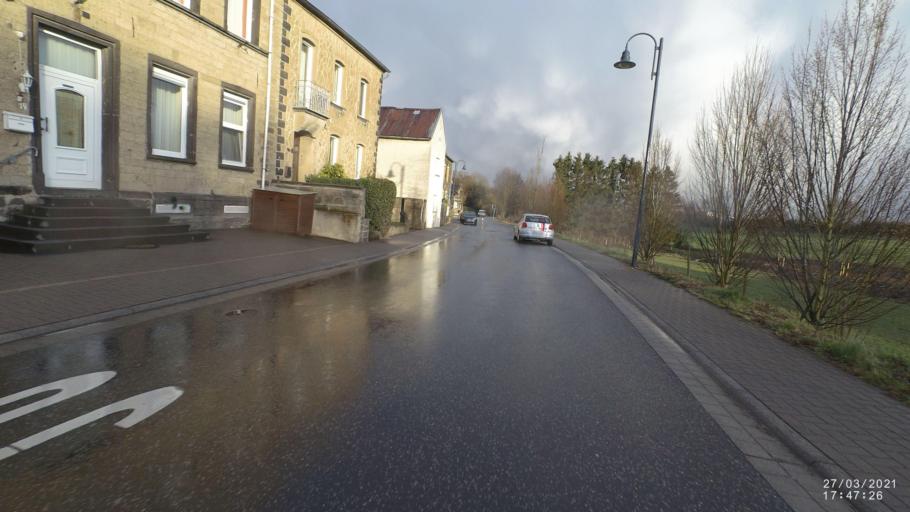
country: DE
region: Rheinland-Pfalz
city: Bell
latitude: 50.3867
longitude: 7.2367
